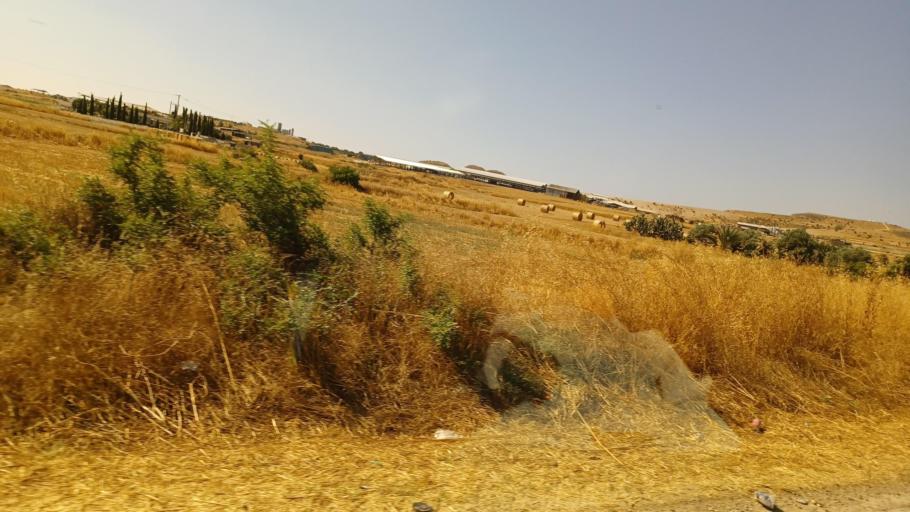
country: CY
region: Larnaka
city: Athienou
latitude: 35.0537
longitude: 33.5293
